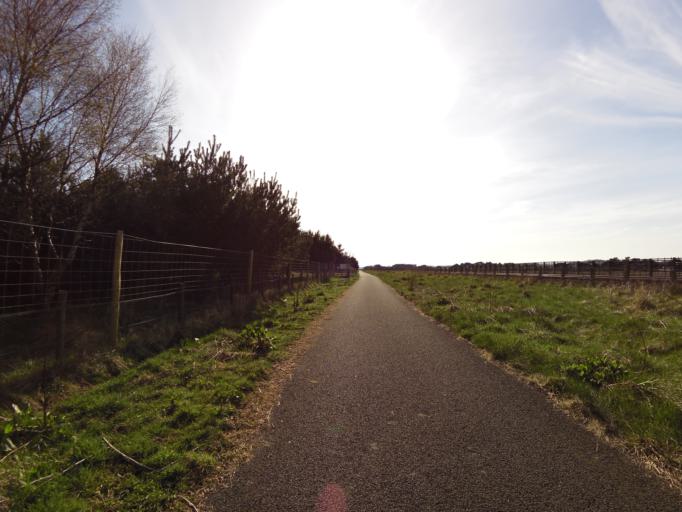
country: GB
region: Scotland
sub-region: Angus
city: Carnoustie
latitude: 56.4914
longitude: -2.7546
